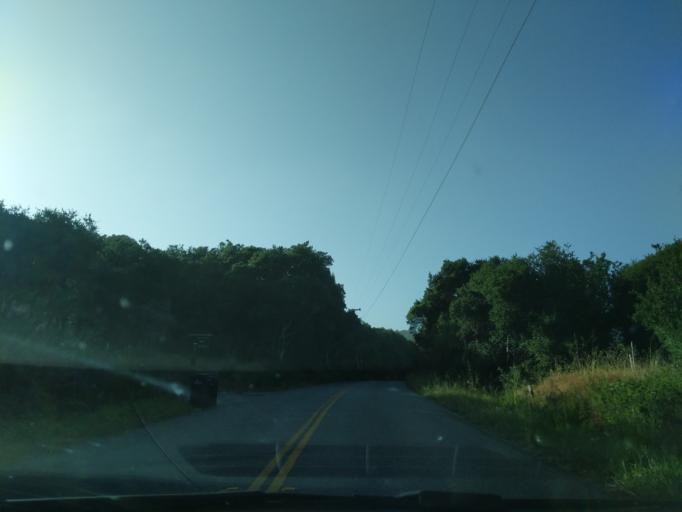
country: US
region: California
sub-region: Monterey County
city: Las Lomas
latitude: 36.8659
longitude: -121.6895
